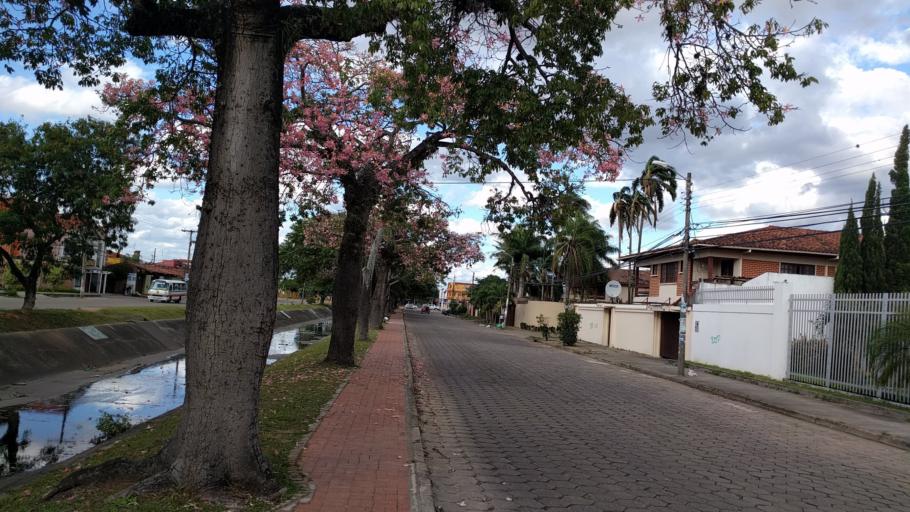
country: BO
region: Santa Cruz
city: Santa Cruz de la Sierra
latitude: -17.7769
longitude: -63.1569
